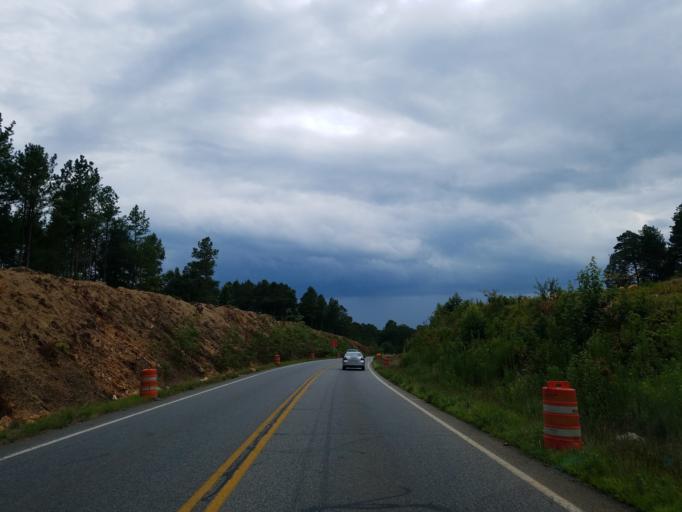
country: US
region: Georgia
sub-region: Bartow County
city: Adairsville
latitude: 34.3740
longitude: -84.9584
